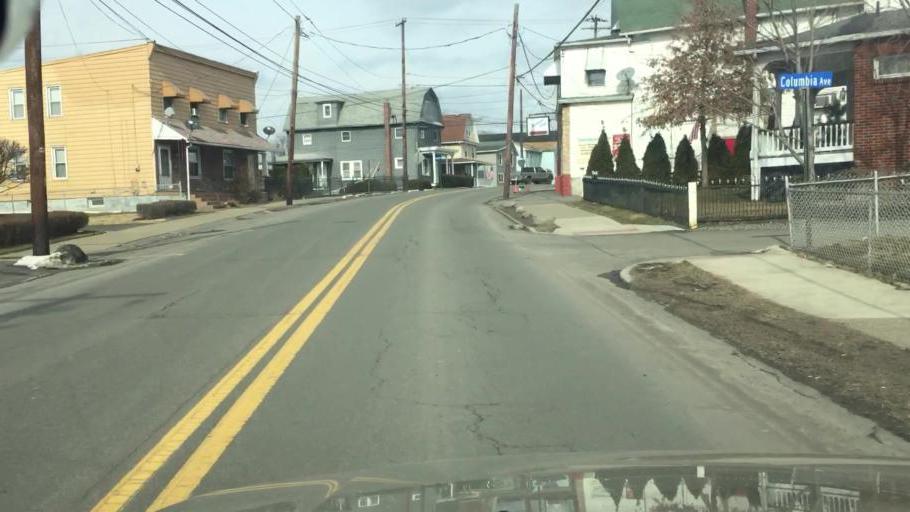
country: US
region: Pennsylvania
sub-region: Luzerne County
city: Ashley
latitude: 41.2211
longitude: -75.8954
